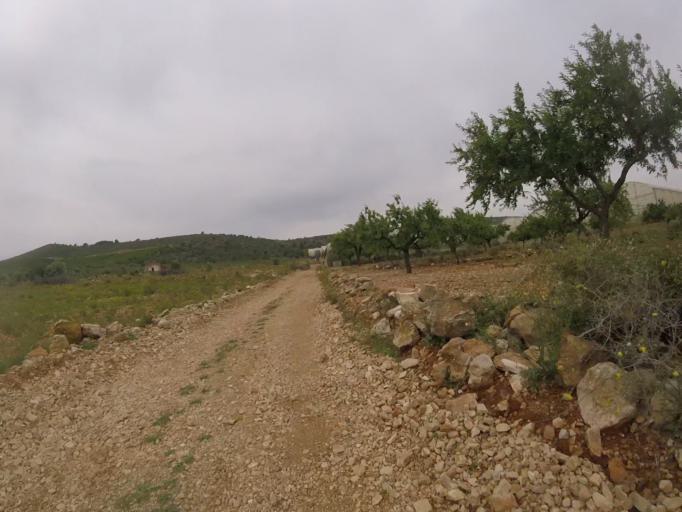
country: ES
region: Valencia
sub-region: Provincia de Castello
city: Alcala de Xivert
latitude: 40.2801
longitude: 0.2556
